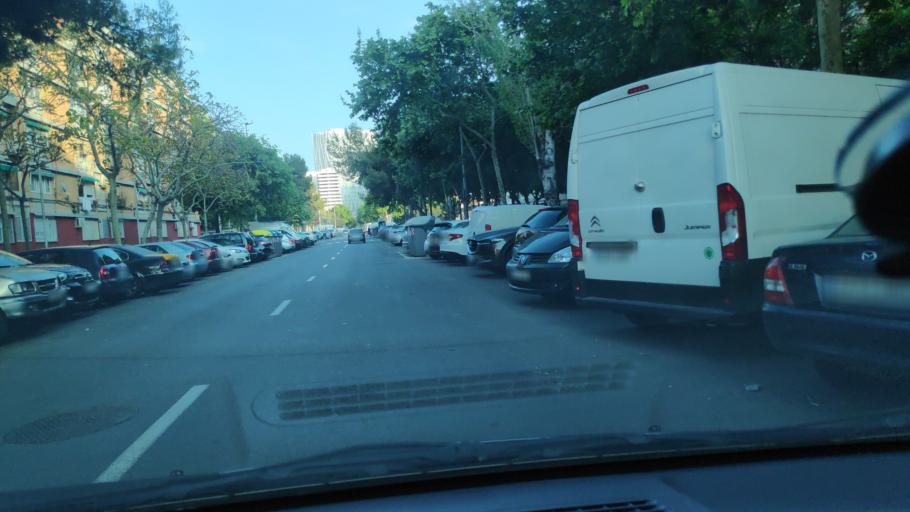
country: ES
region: Catalonia
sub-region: Provincia de Barcelona
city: Sant Adria de Besos
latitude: 41.4164
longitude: 2.2145
